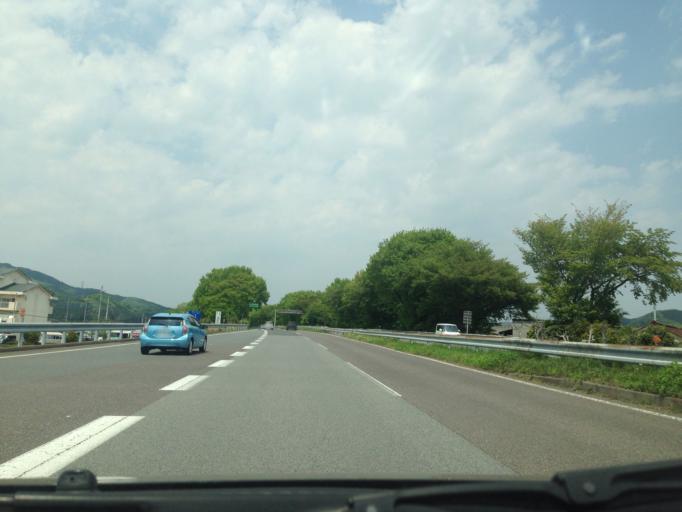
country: JP
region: Tochigi
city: Utsunomiya-shi
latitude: 36.6382
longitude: 139.8449
